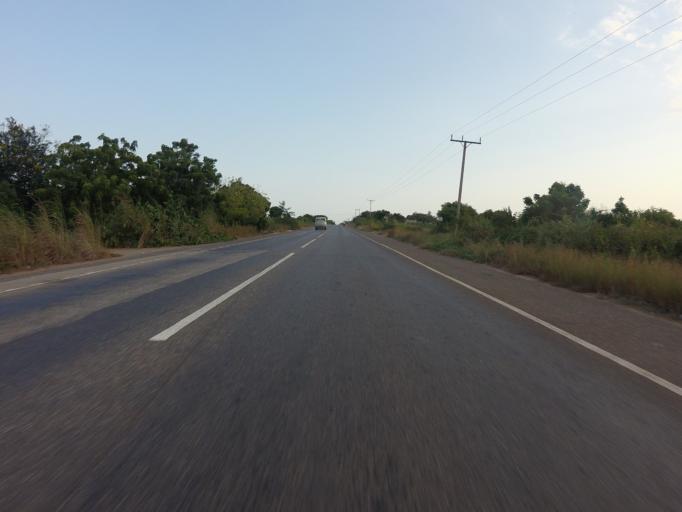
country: GH
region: Volta
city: Anloga
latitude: 6.0670
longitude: 0.6045
